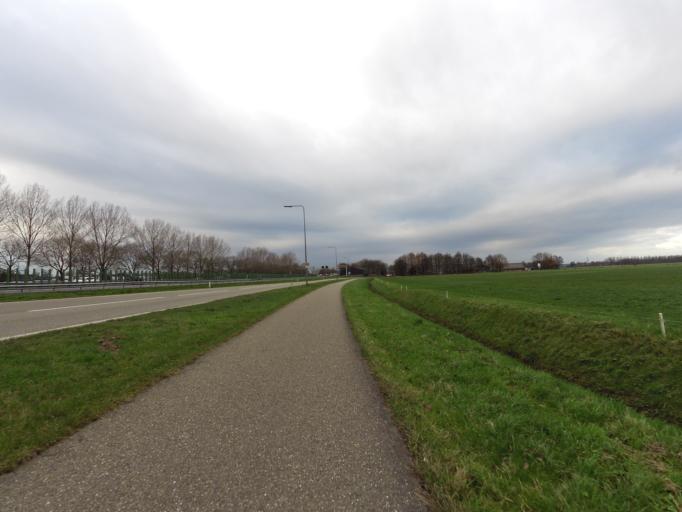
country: NL
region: Gelderland
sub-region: Gemeente Zevenaar
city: Zevenaar
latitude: 51.9393
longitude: 6.0897
